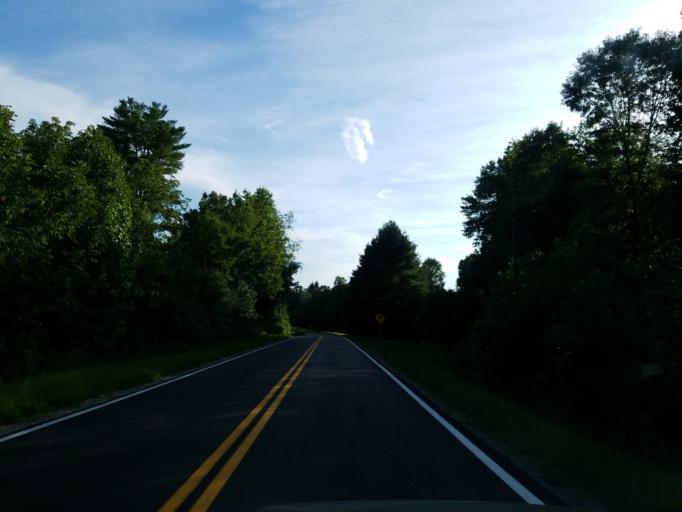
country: US
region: Georgia
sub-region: White County
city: Cleveland
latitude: 34.5940
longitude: -83.8734
